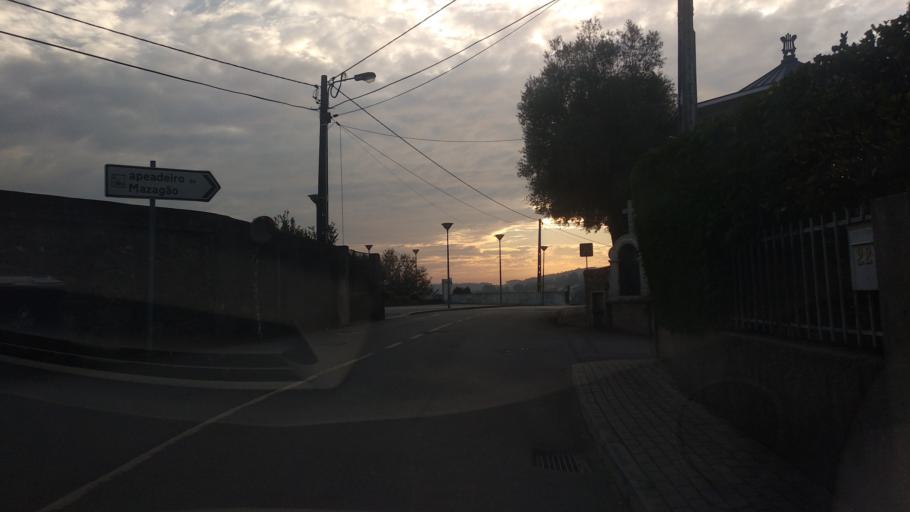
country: PT
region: Braga
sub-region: Braga
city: Braga
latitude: 41.5256
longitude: -8.4560
